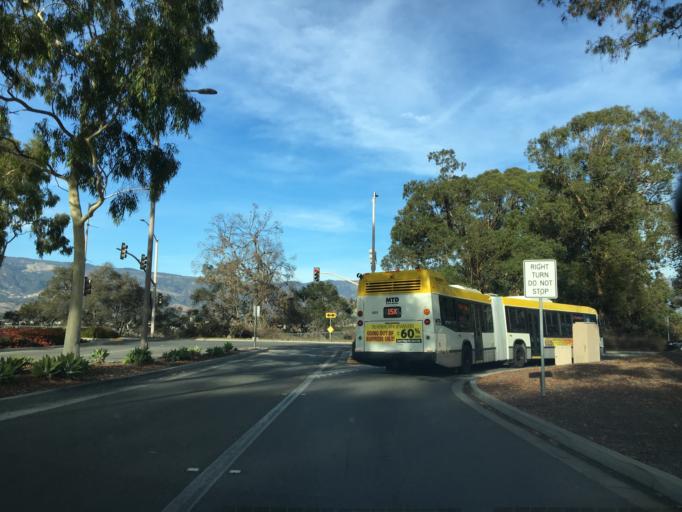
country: US
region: California
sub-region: Santa Barbara County
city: Isla Vista
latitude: 34.4188
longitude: -119.8479
